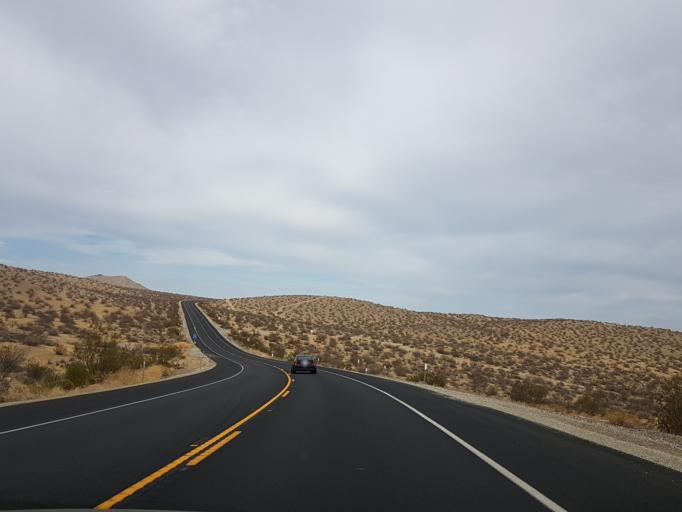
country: US
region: California
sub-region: Kern County
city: Ridgecrest
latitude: 35.4536
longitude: -117.6545
